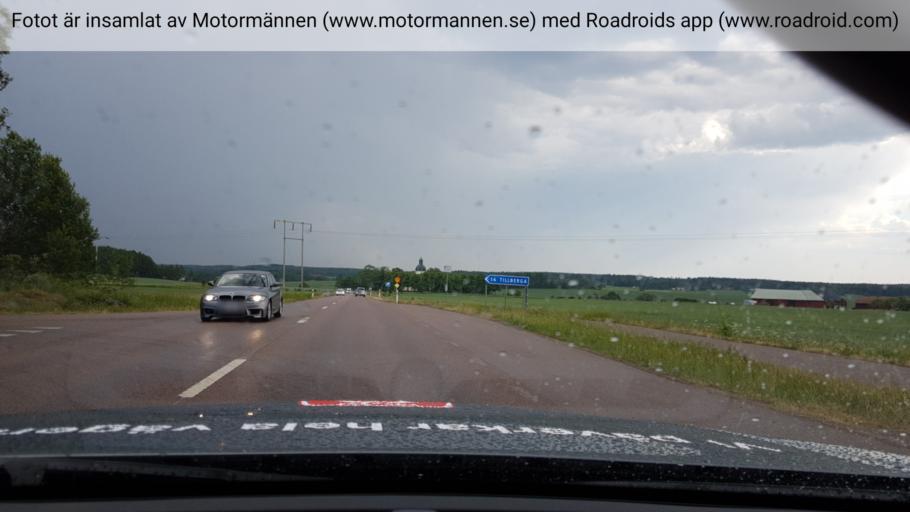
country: SE
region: Vaestmanland
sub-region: Vasteras
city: Skultuna
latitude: 59.7057
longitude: 16.4300
